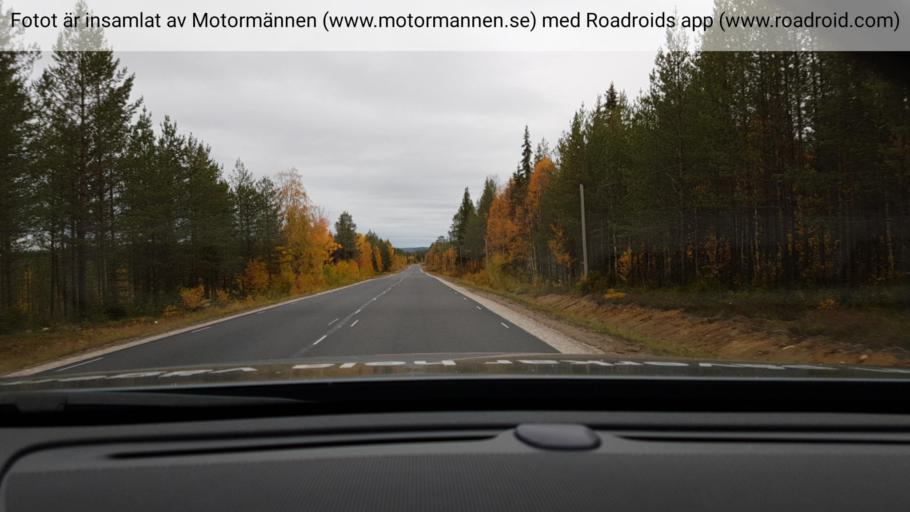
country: SE
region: Norrbotten
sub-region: Overkalix Kommun
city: OEverkalix
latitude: 66.3780
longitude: 22.8363
